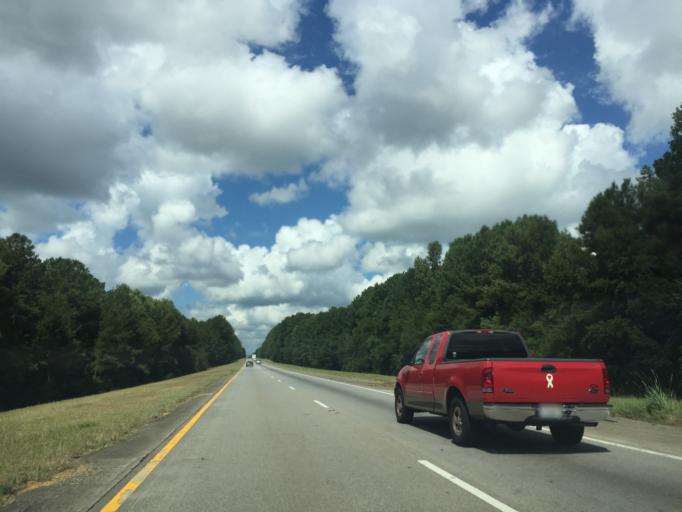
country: US
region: Georgia
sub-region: Candler County
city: Metter
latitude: 32.3847
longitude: -82.2431
